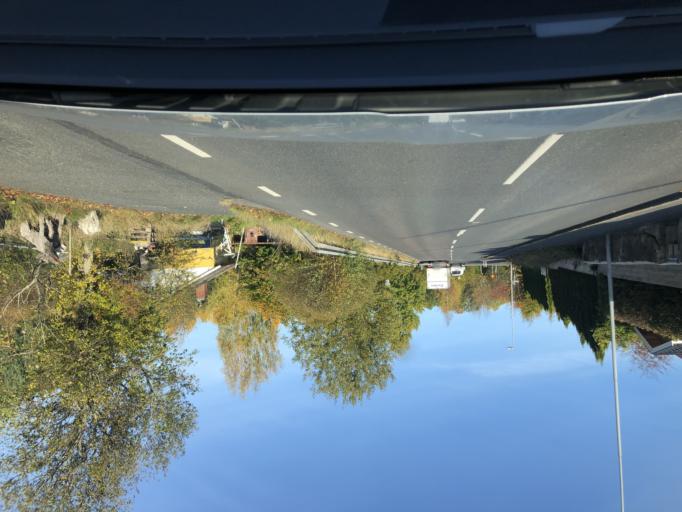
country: SE
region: Joenkoeping
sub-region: Jonkopings Kommun
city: Jonkoping
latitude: 57.7736
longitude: 14.1296
